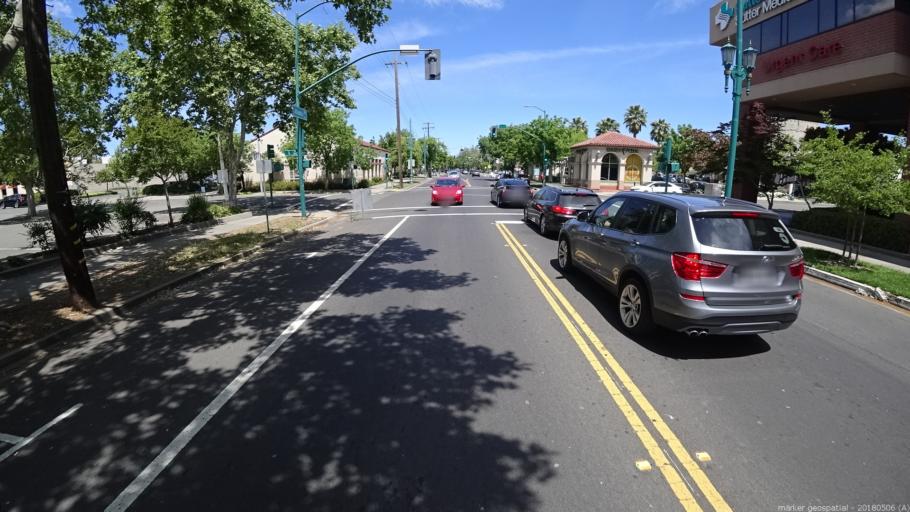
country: US
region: California
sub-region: Sacramento County
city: Sacramento
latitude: 38.5703
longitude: -121.4663
